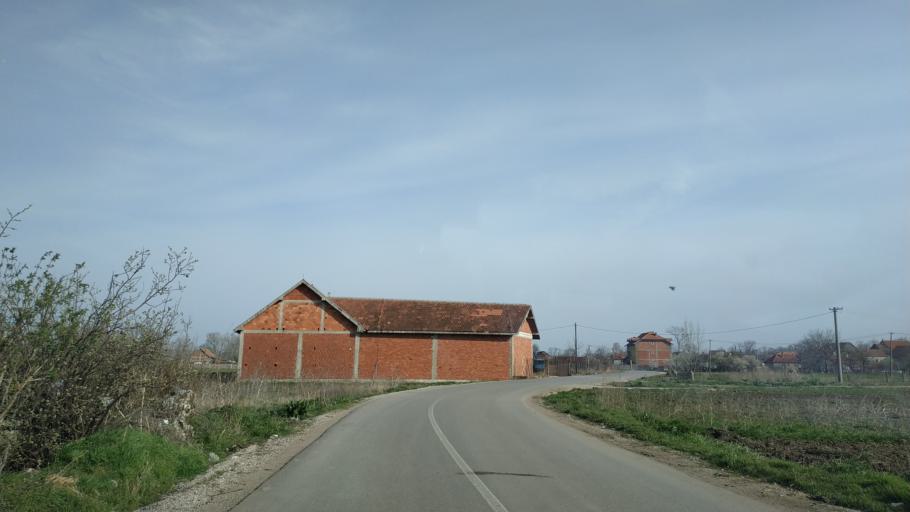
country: RS
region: Central Serbia
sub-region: Nisavski Okrug
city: Aleksinac
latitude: 43.5177
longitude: 21.6888
